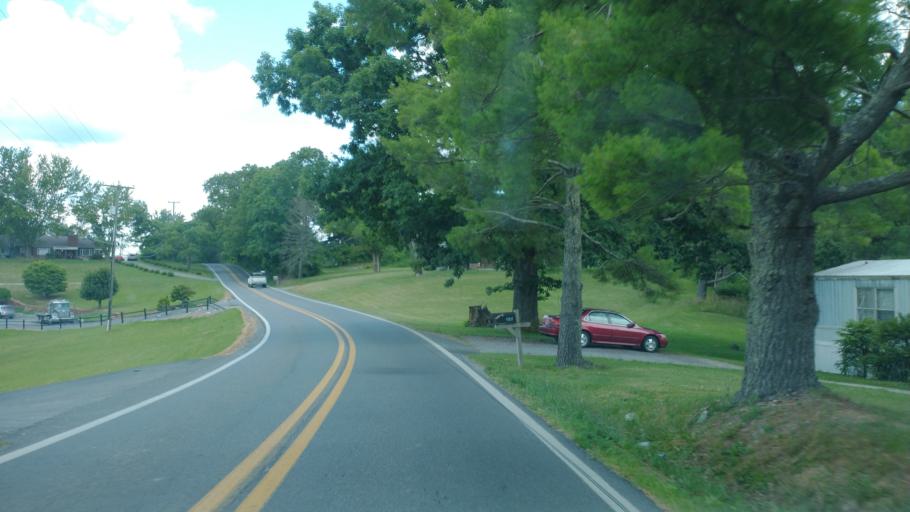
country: US
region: West Virginia
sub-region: Mercer County
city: Athens
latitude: 37.3997
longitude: -81.0610
